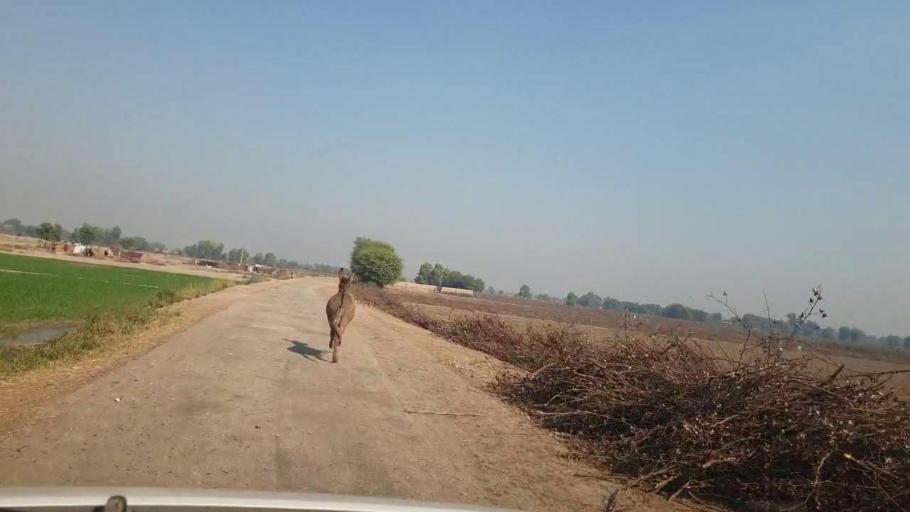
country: PK
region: Sindh
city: Bhan
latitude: 26.6136
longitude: 67.7605
